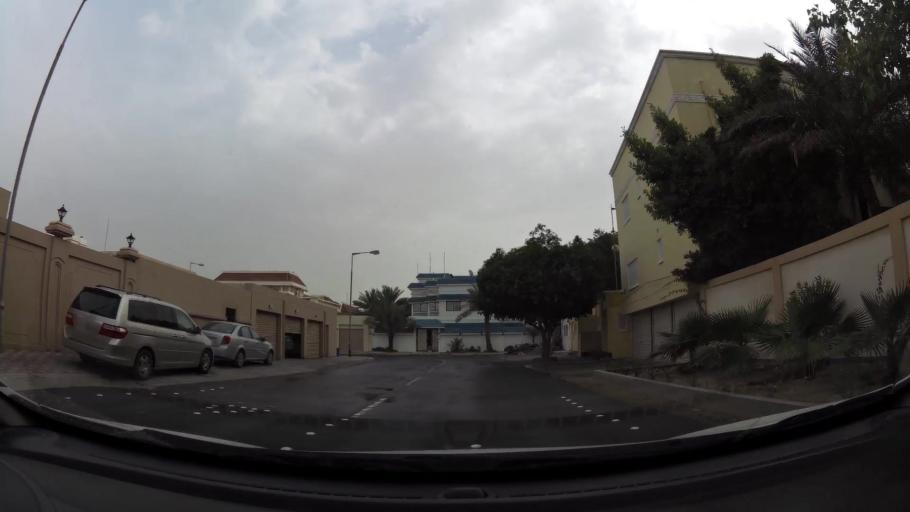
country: BH
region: Northern
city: Ar Rifa'
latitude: 26.1329
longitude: 50.5452
